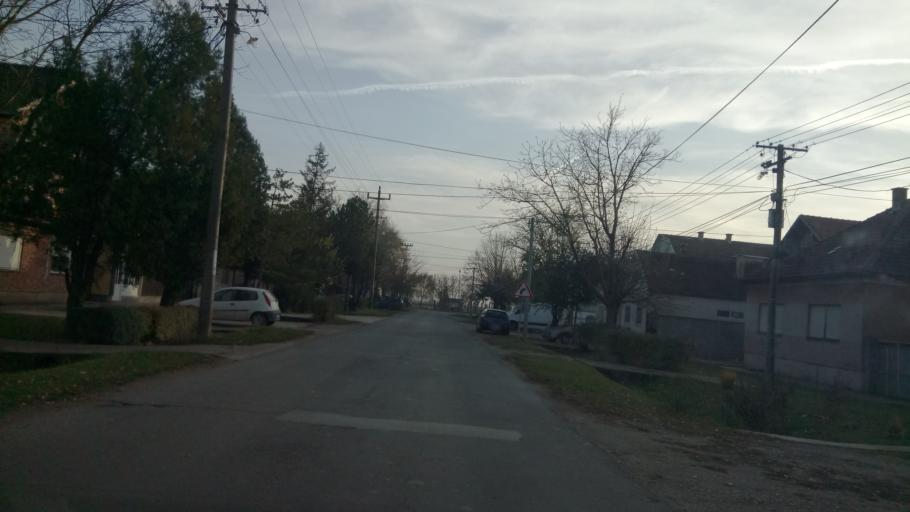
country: RS
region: Autonomna Pokrajina Vojvodina
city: Nova Pazova
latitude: 44.9367
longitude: 20.2152
